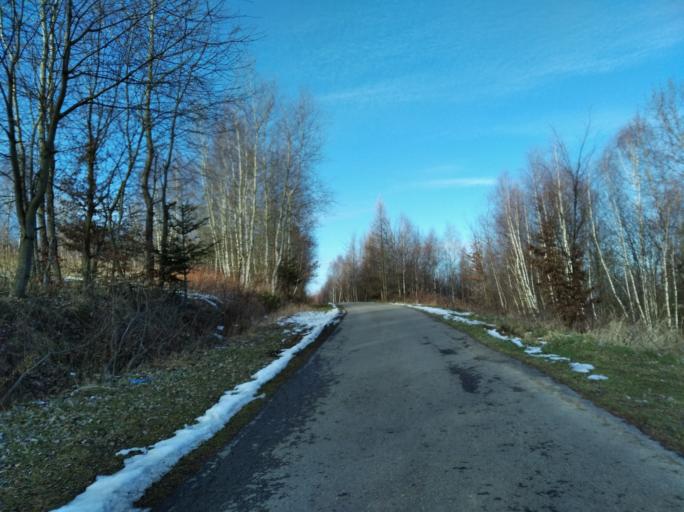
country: PL
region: Subcarpathian Voivodeship
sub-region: Powiat strzyzowski
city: Gwoznica Gorna
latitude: 49.8189
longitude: 21.9900
